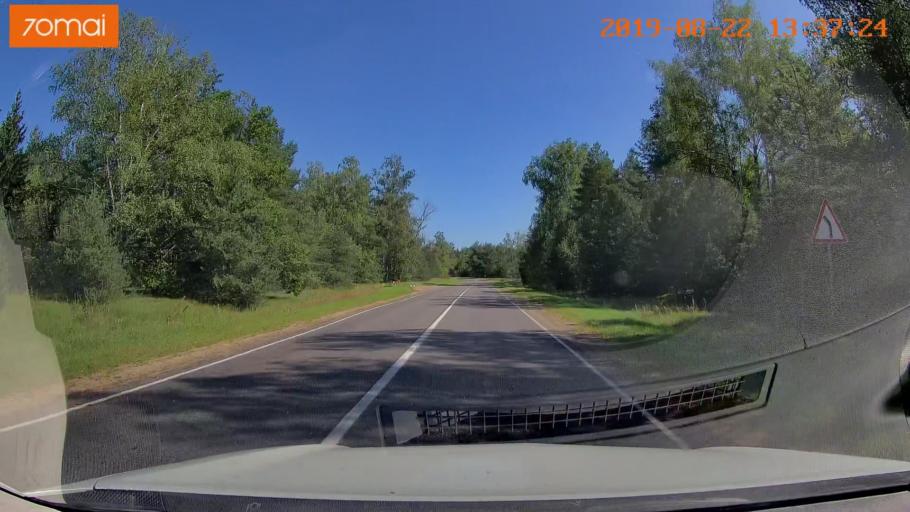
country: BY
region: Minsk
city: Staryya Darohi
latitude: 53.2168
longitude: 28.2982
